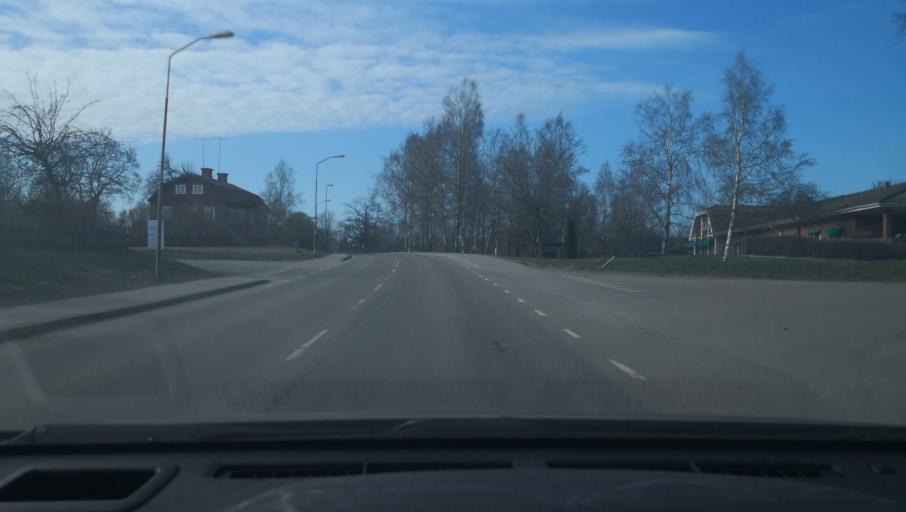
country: SE
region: Uppsala
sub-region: Heby Kommun
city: Heby
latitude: 59.9398
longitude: 16.8641
